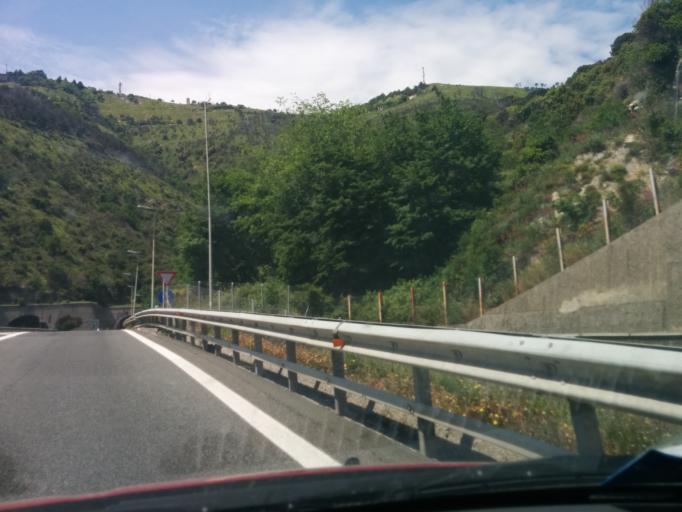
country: IT
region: Liguria
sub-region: Provincia di Genova
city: Genoa
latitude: 44.4375
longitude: 8.9408
